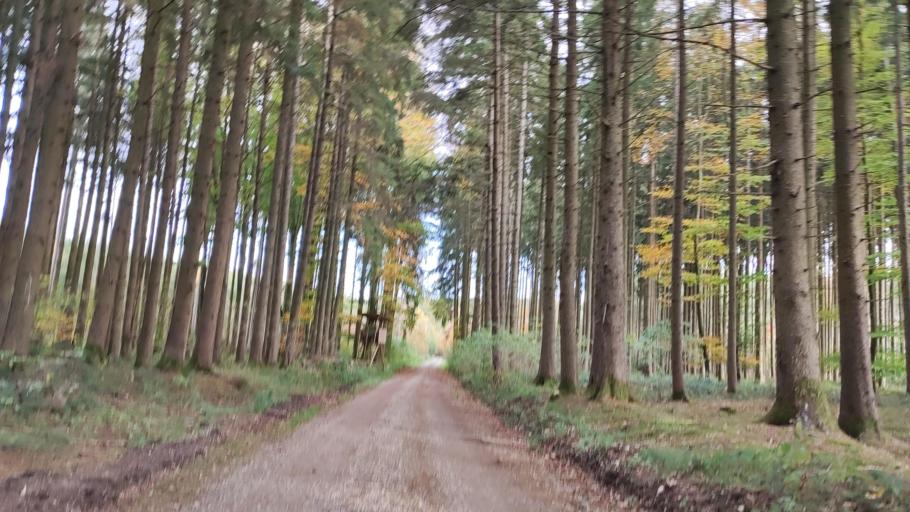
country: DE
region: Bavaria
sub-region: Swabia
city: Munsterhausen
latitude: 48.3226
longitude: 10.4837
